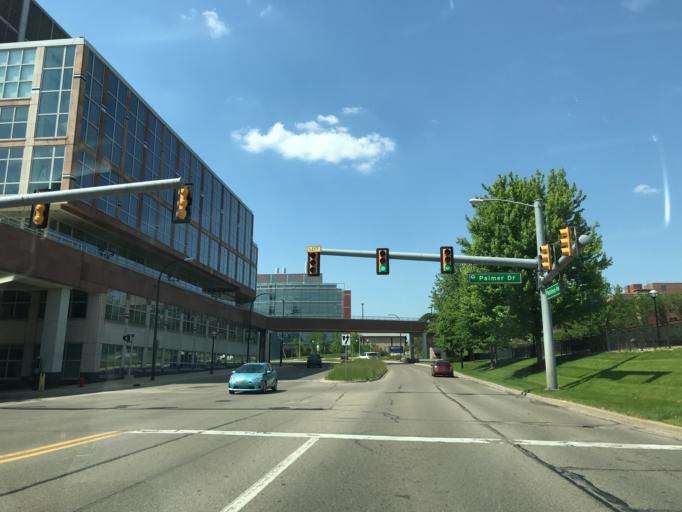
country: US
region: Michigan
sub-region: Washtenaw County
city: Ann Arbor
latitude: 42.2799
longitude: -83.7334
